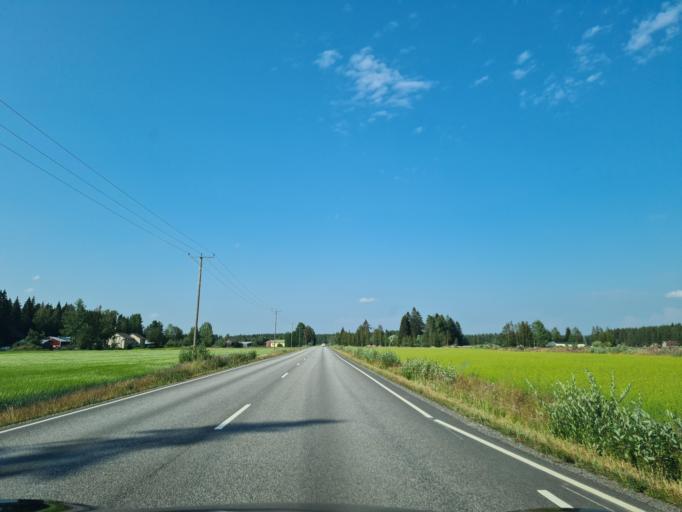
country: FI
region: Satakunta
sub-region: Pohjois-Satakunta
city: Kankaanpaeae
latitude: 61.9141
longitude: 22.5030
